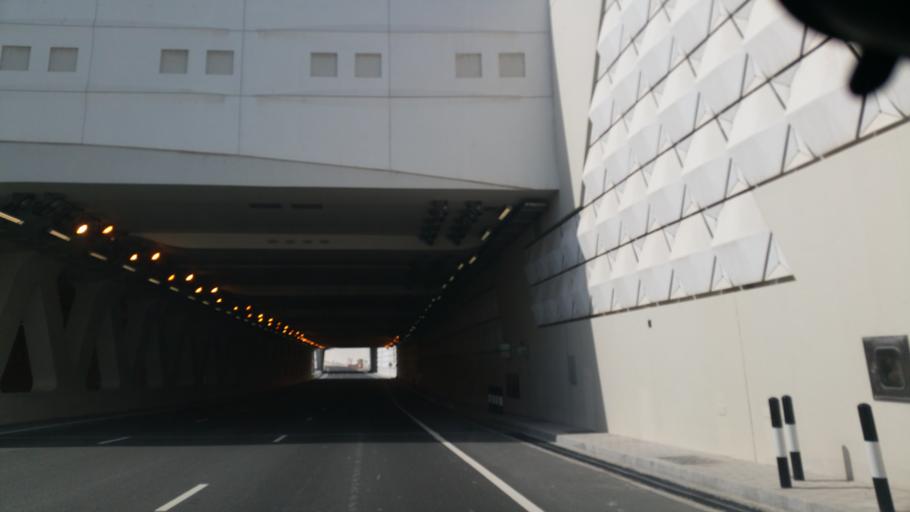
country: QA
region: Baladiyat Umm Salal
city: Umm Salal Muhammad
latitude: 25.4058
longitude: 51.5128
